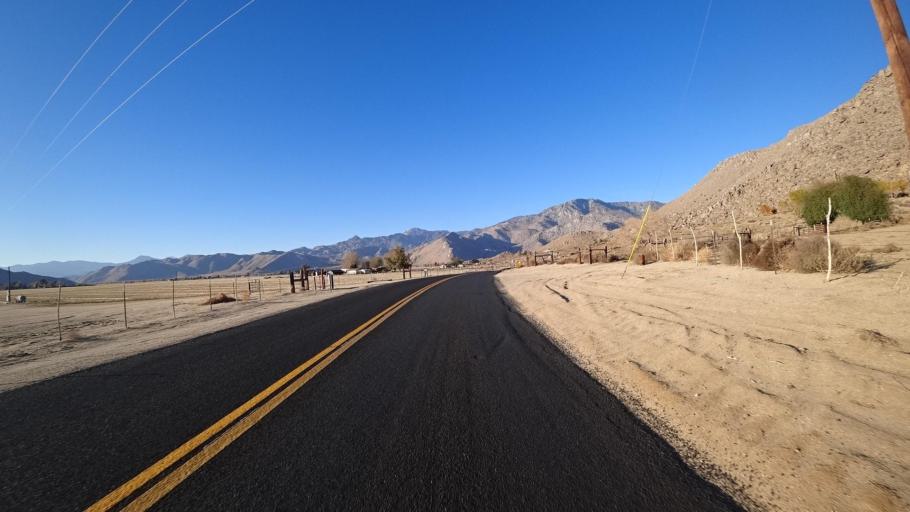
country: US
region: California
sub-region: Kern County
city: Weldon
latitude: 35.6526
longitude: -118.2535
